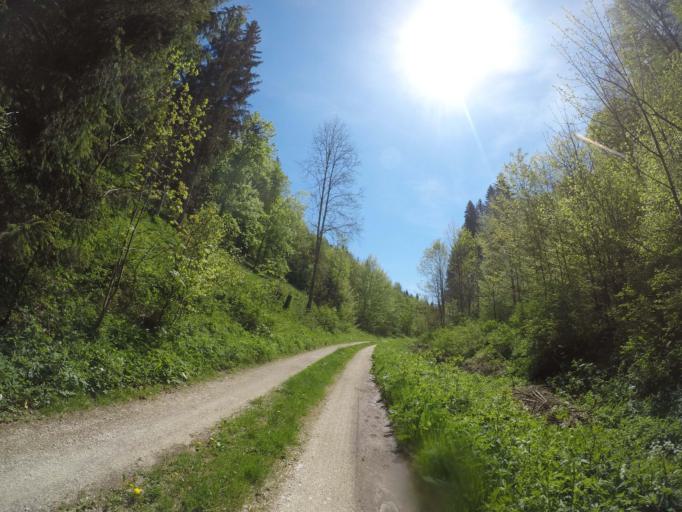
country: DE
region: Baden-Wuerttemberg
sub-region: Tuebingen Region
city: Schelklingen
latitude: 48.4223
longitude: 9.7015
